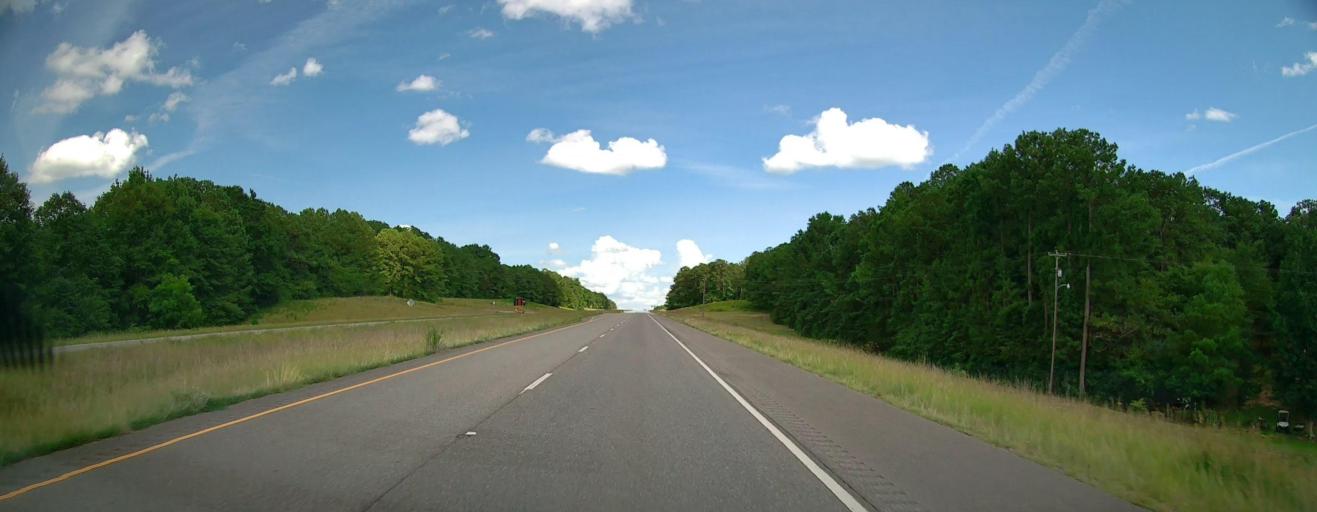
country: US
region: Alabama
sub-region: Pickens County
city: Reform
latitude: 33.3997
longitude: -88.0651
